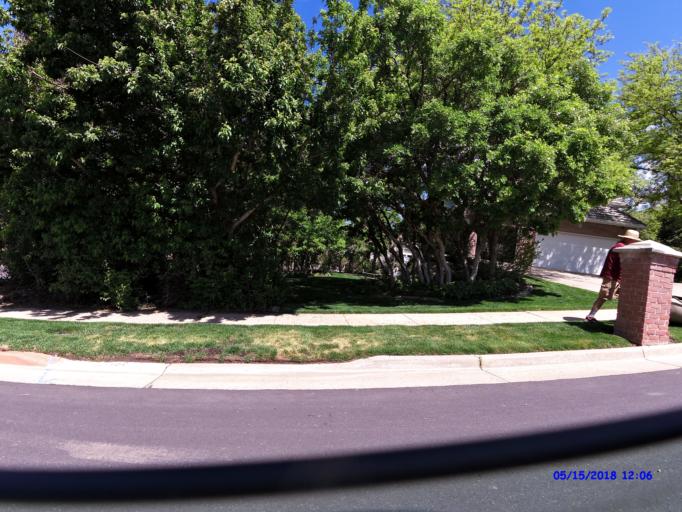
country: US
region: Utah
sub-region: Weber County
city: South Ogden
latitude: 41.1826
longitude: -111.9332
